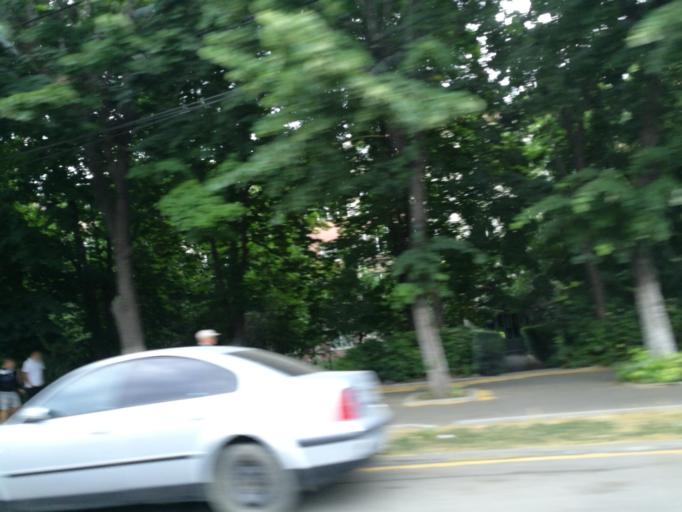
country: RO
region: Constanta
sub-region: Municipiul Constanta
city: Constanta
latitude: 44.1988
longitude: 28.6314
